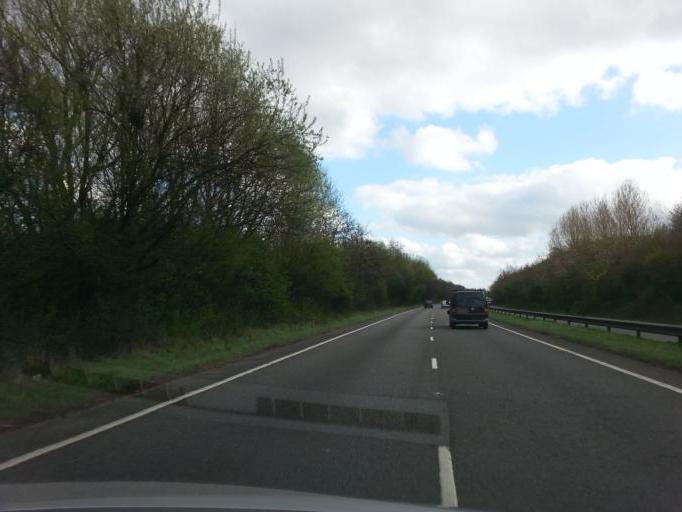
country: GB
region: England
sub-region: Hampshire
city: Farnborough
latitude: 51.2895
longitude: -0.7361
